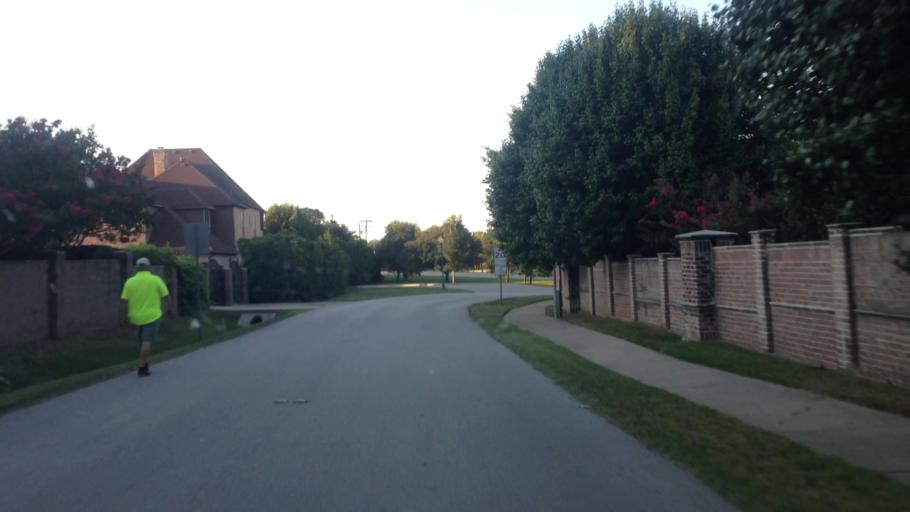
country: US
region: Texas
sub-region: Tarrant County
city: Southlake
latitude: 32.9286
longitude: -97.1283
